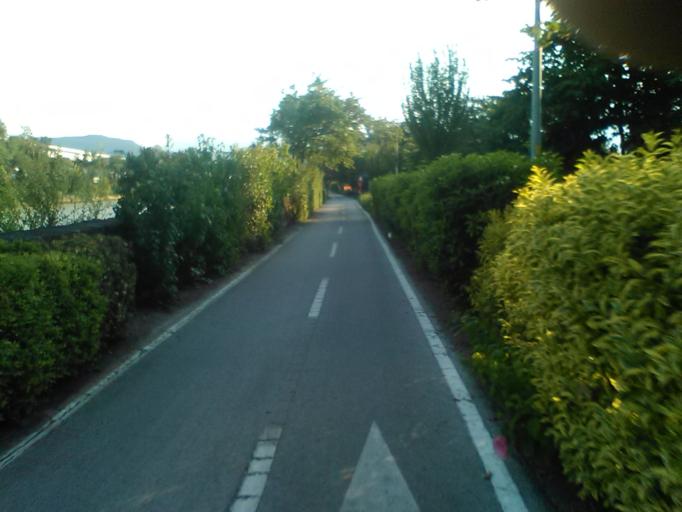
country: IT
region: Trentino-Alto Adige
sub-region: Bolzano
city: Bolzano
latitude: 46.4853
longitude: 11.3274
